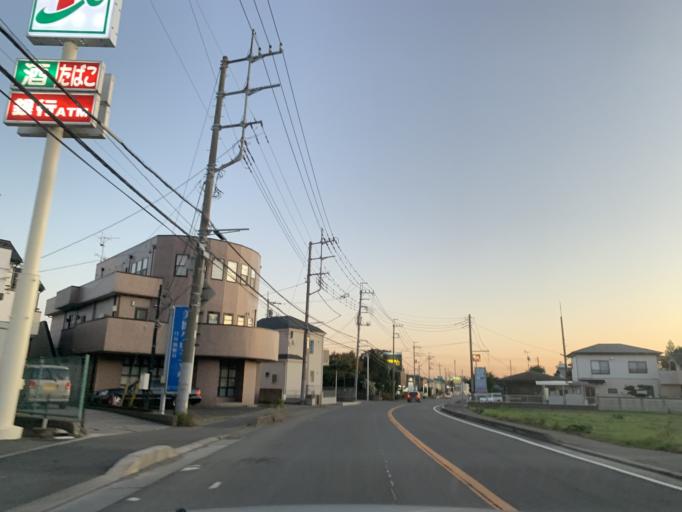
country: JP
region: Chiba
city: Nagareyama
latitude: 35.9008
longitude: 139.9023
